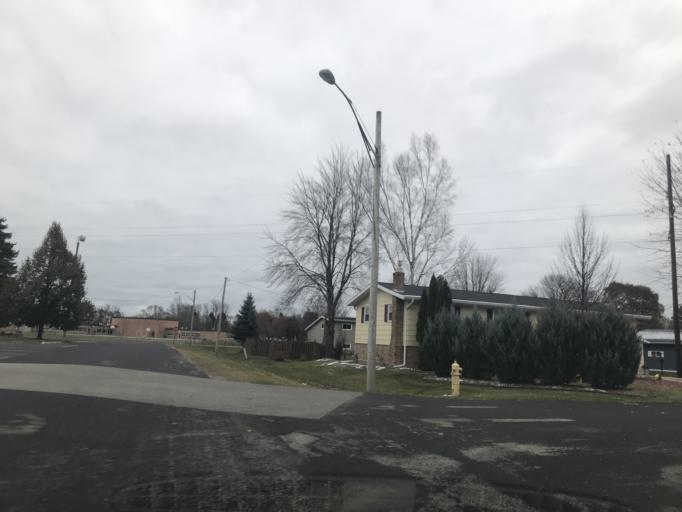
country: US
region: Wisconsin
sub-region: Marinette County
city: Marinette
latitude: 45.0955
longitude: -87.6523
